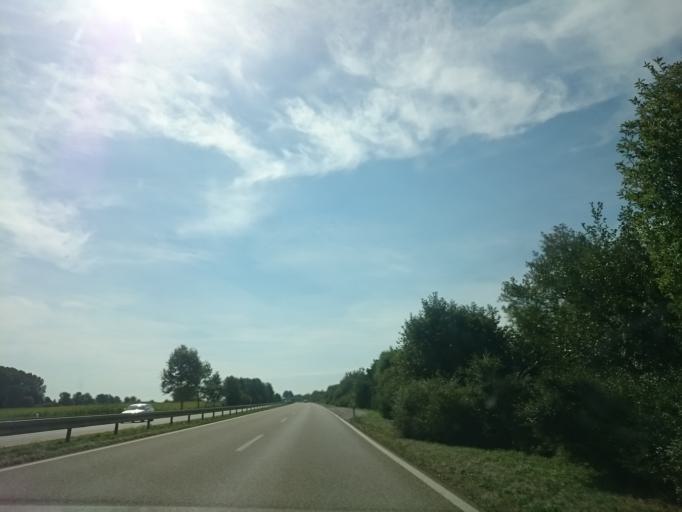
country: DE
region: Bavaria
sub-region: Swabia
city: Mertingen
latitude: 48.6339
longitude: 10.8353
